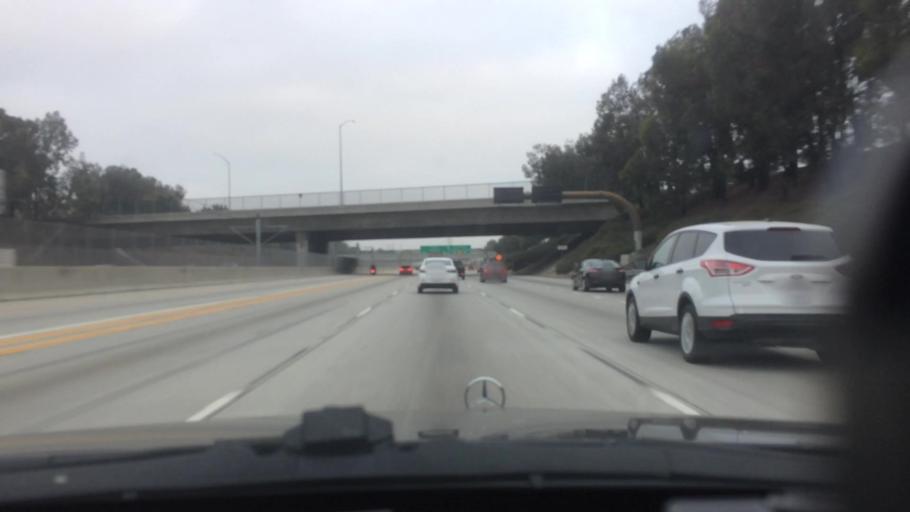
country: US
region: California
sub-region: Los Angeles County
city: Paramount
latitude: 33.9122
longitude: -118.1585
